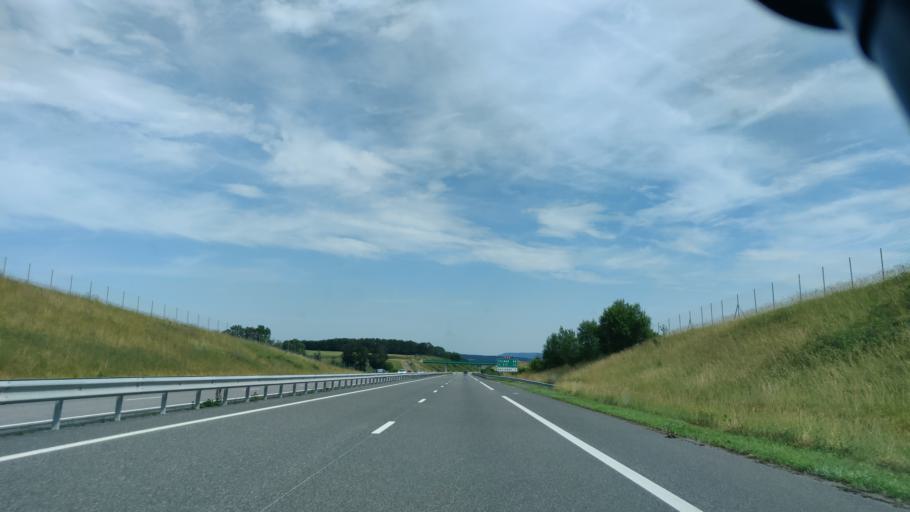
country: FR
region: Lorraine
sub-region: Departement de Meurthe-et-Moselle
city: Baccarat
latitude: 48.4974
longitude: 6.6970
